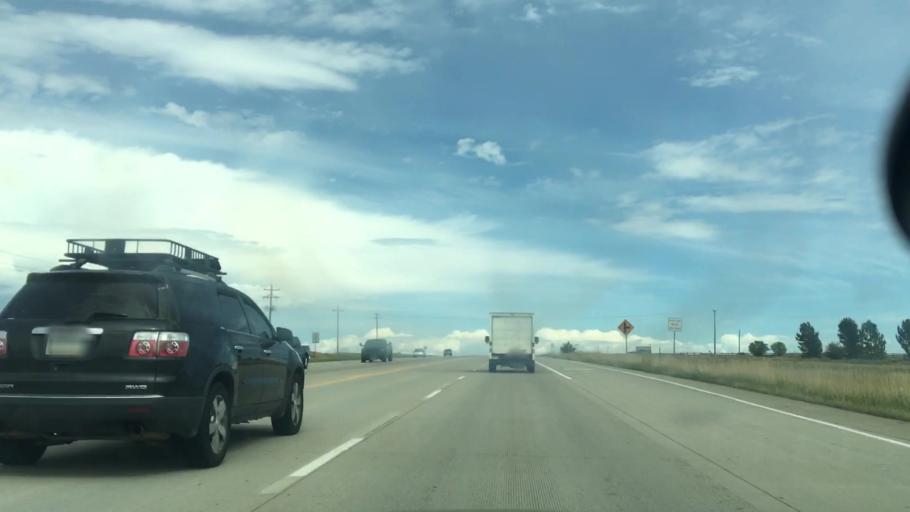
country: US
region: Colorado
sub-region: Larimer County
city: Berthoud
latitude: 40.2814
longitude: -105.1022
